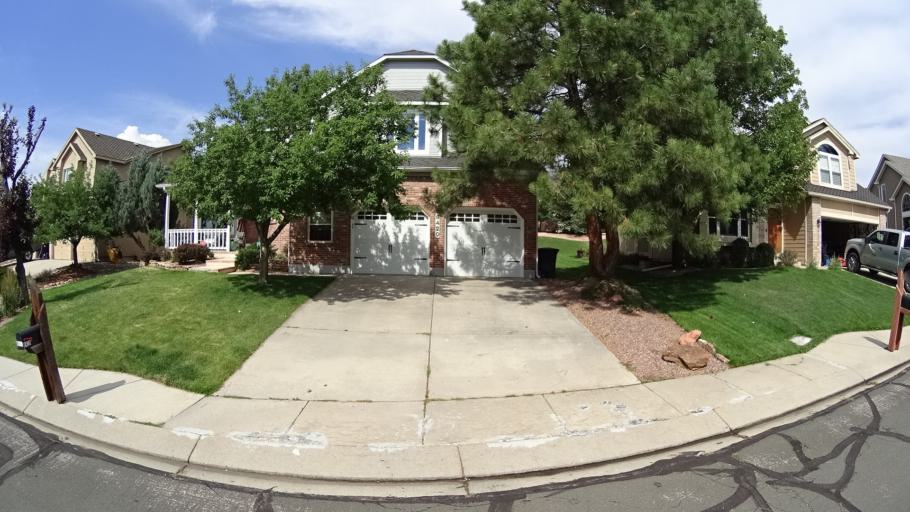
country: US
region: Colorado
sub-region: El Paso County
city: Air Force Academy
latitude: 38.9520
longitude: -104.8601
